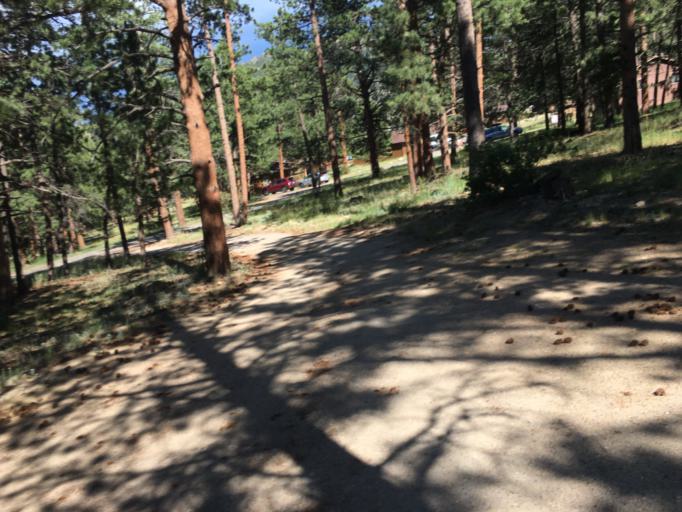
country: US
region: Colorado
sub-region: Larimer County
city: Estes Park
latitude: 40.3422
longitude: -105.5775
